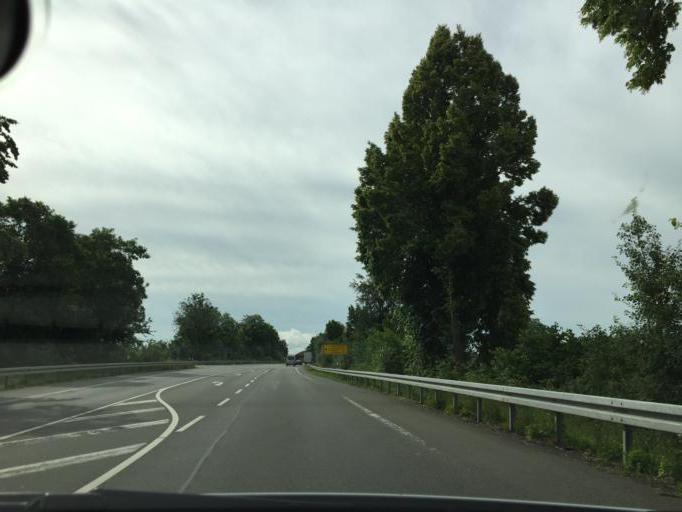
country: DE
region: North Rhine-Westphalia
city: Warburg
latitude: 51.5351
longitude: 9.1372
